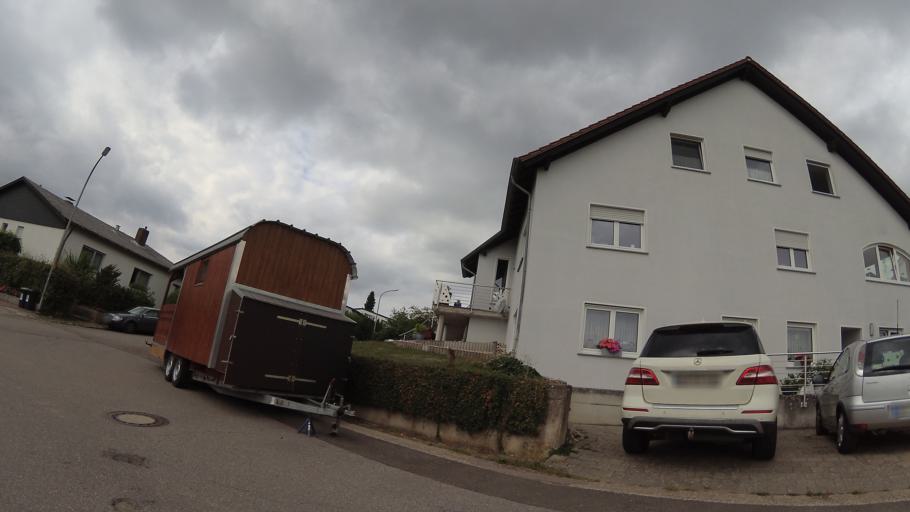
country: DE
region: Saarland
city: Kleinblittersdorf
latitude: 49.1704
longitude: 7.0872
